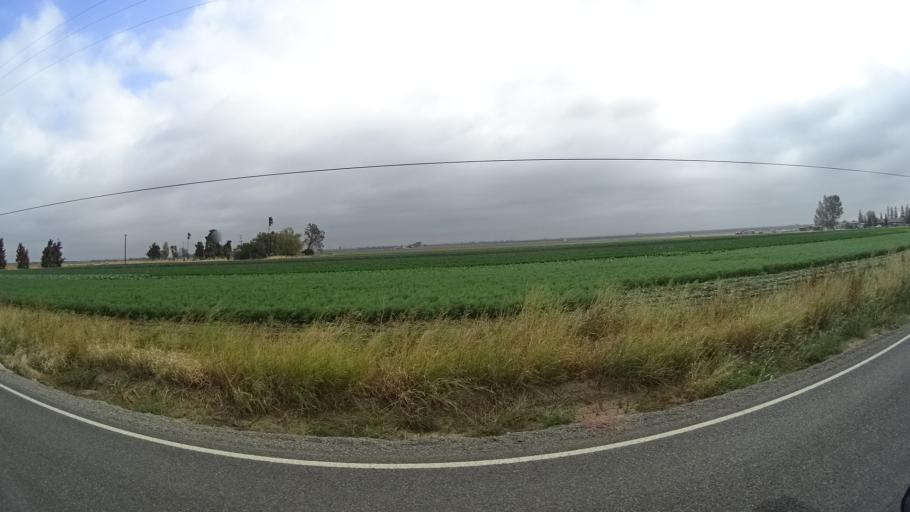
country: US
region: California
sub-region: Yolo County
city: Esparto
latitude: 38.7436
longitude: -122.0451
